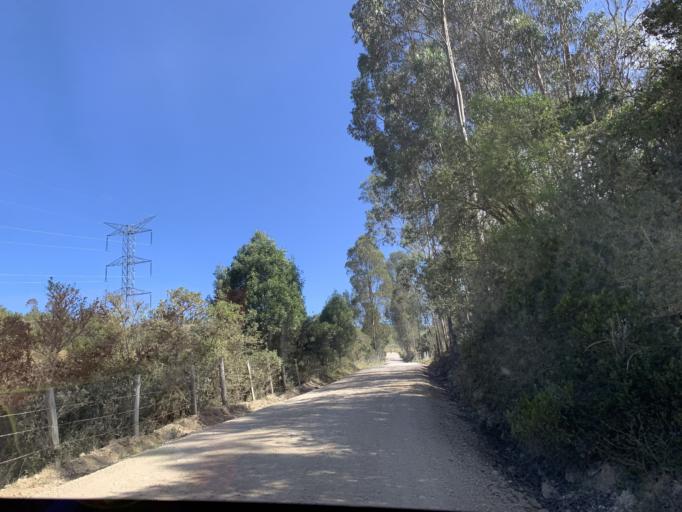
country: CO
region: Boyaca
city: Tuta
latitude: 5.6983
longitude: -73.1484
